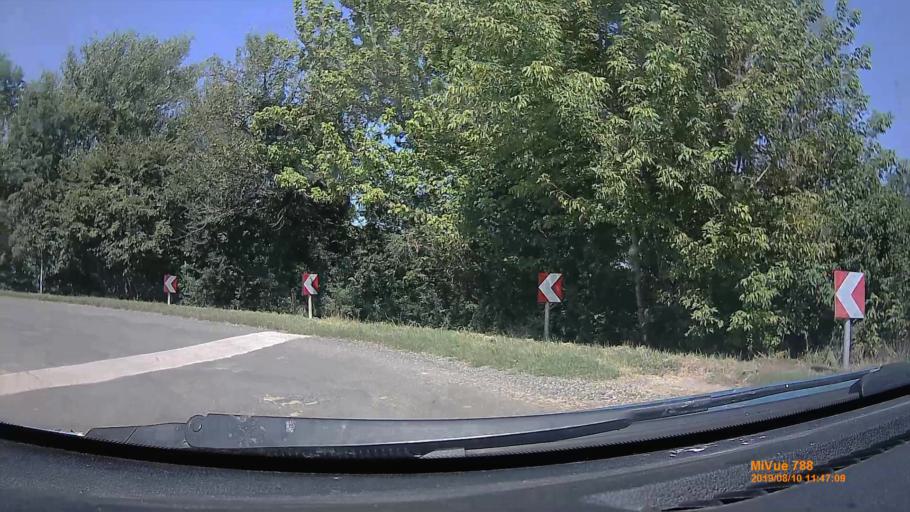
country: HU
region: Somogy
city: Somogyvar
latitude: 46.5103
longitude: 17.7413
